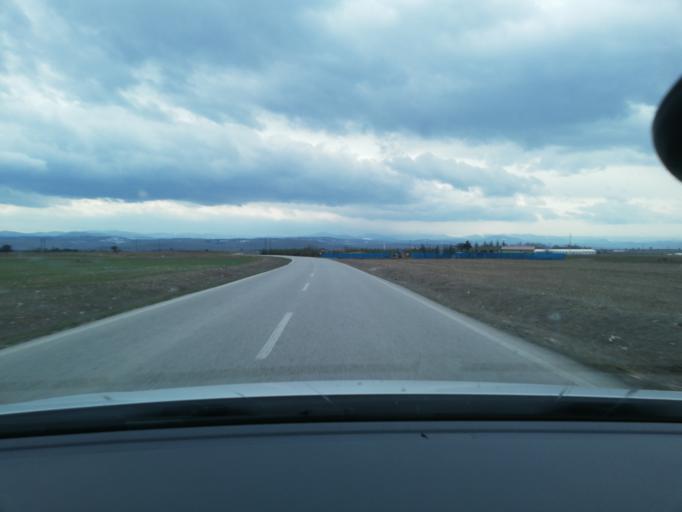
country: TR
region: Bolu
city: Gerede
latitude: 40.7704
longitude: 32.2030
